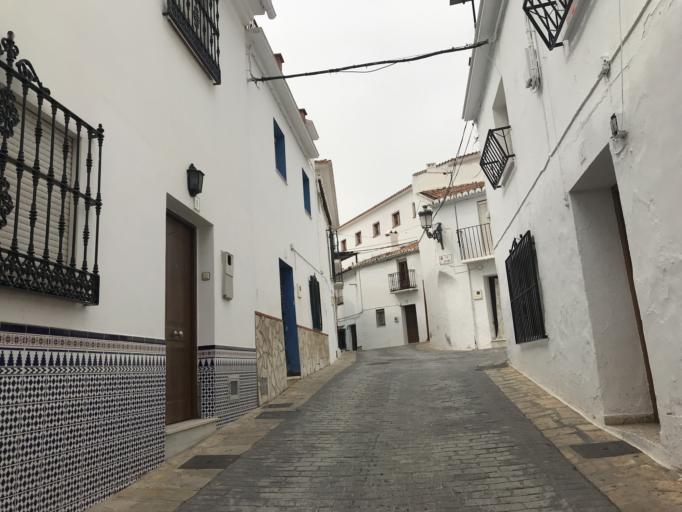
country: ES
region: Andalusia
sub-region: Provincia de Malaga
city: Alcaucin
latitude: 36.9022
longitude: -4.1140
